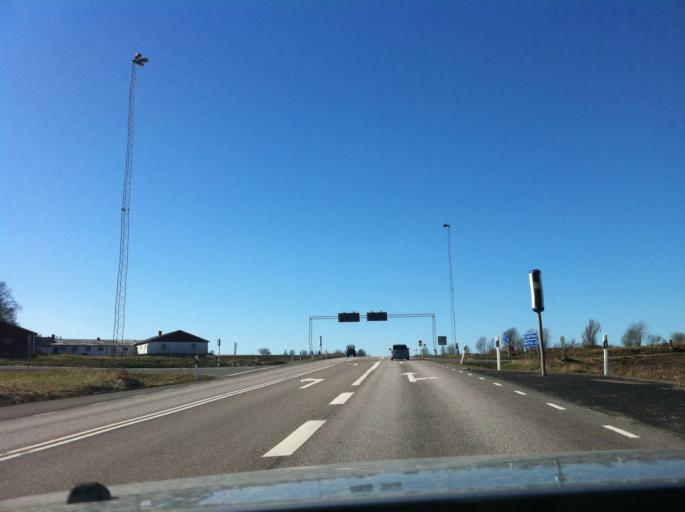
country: SE
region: Vaestra Goetaland
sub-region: Falkopings Kommun
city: Falkoeping
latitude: 58.1402
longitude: 13.6361
